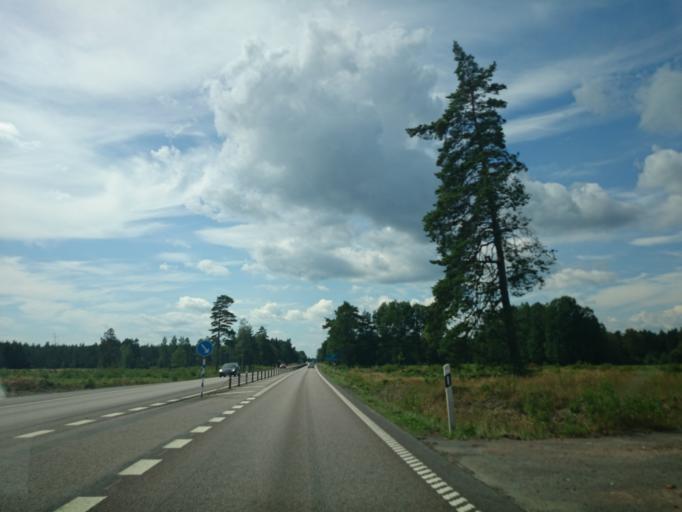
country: SE
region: Kalmar
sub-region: Monsteras Kommun
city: Moensteras
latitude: 57.0759
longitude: 16.4794
